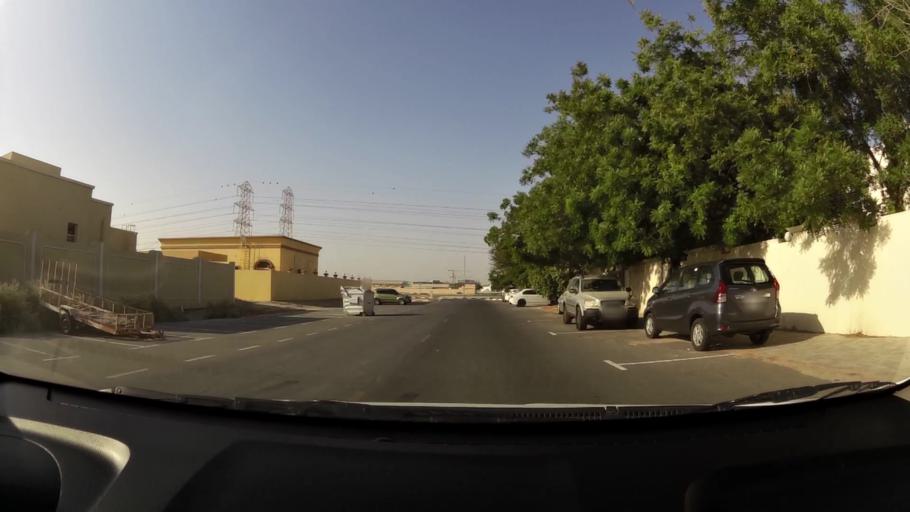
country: AE
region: Ash Shariqah
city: Sharjah
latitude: 25.2707
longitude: 55.3905
